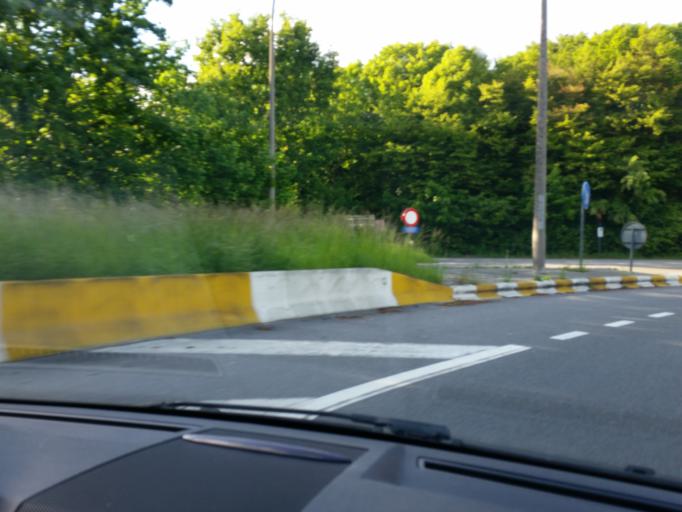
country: BE
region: Flanders
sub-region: Provincie Oost-Vlaanderen
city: Ledeberg
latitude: 51.0337
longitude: 3.7503
